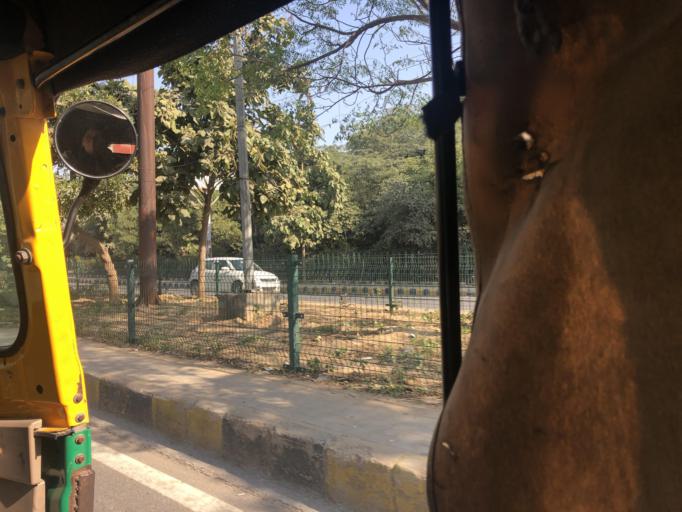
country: IN
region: Haryana
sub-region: Gurgaon
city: Gurgaon
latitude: 28.4302
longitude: 77.0913
